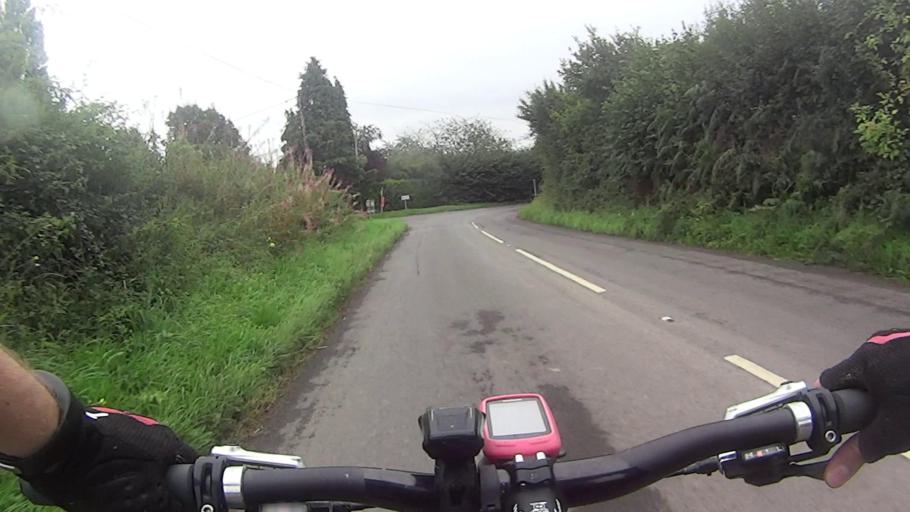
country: GB
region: England
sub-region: Worcestershire
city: Tenbury Wells
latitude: 52.2903
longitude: -2.5656
